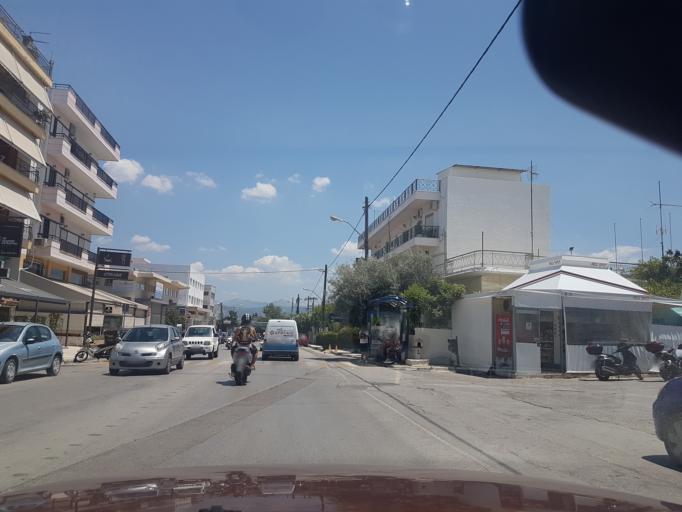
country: GR
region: Central Greece
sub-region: Nomos Evvoias
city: Chalkida
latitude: 38.4696
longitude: 23.6095
